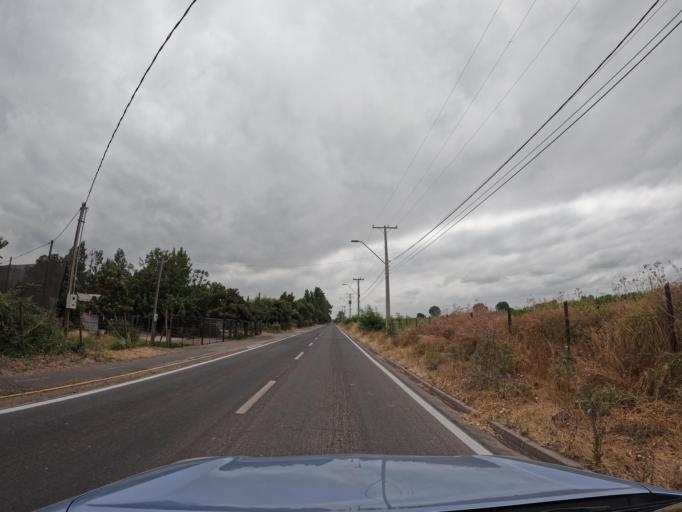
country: CL
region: O'Higgins
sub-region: Provincia de Colchagua
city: Chimbarongo
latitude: -34.7335
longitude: -71.0622
